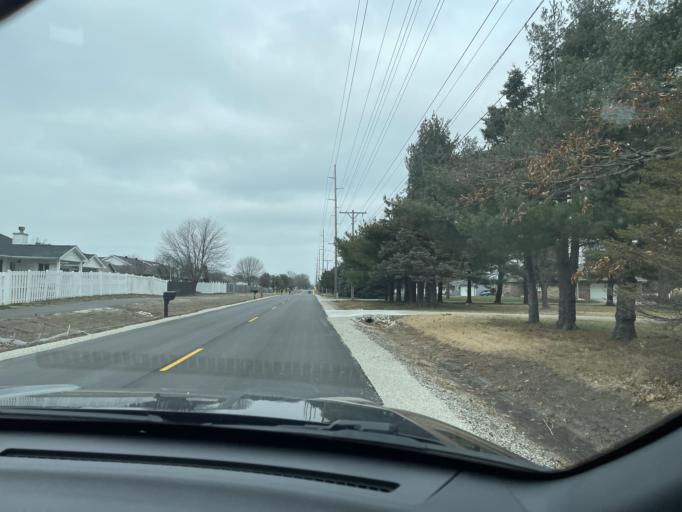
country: US
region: Illinois
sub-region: Sangamon County
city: Rochester
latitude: 39.7565
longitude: -89.5786
